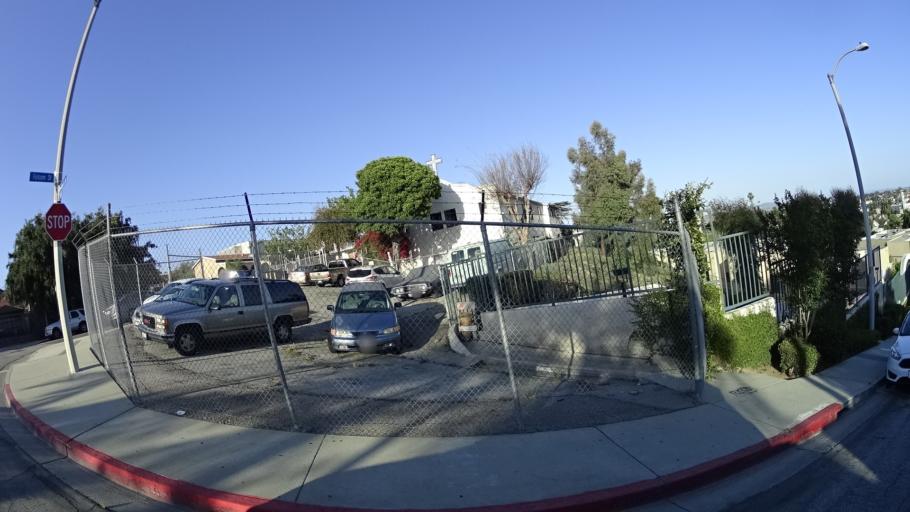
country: US
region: California
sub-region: Los Angeles County
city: Belvedere
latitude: 34.0448
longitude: -118.1832
